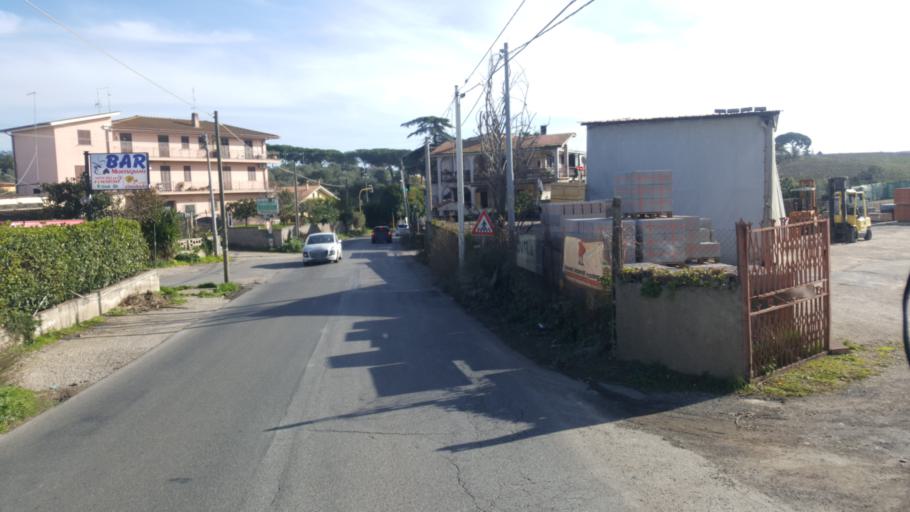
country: IT
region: Latium
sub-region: Citta metropolitana di Roma Capitale
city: Mantiglia di Ardea
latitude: 41.6797
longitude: 12.6227
